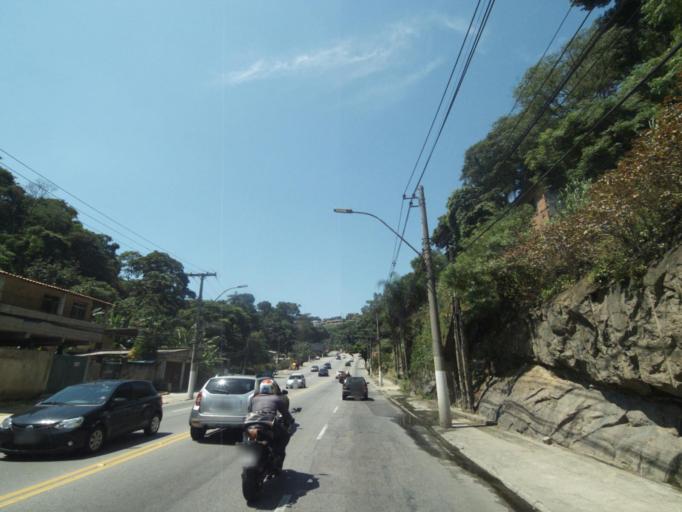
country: BR
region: Rio de Janeiro
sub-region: Niteroi
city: Niteroi
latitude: -22.9112
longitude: -43.0726
